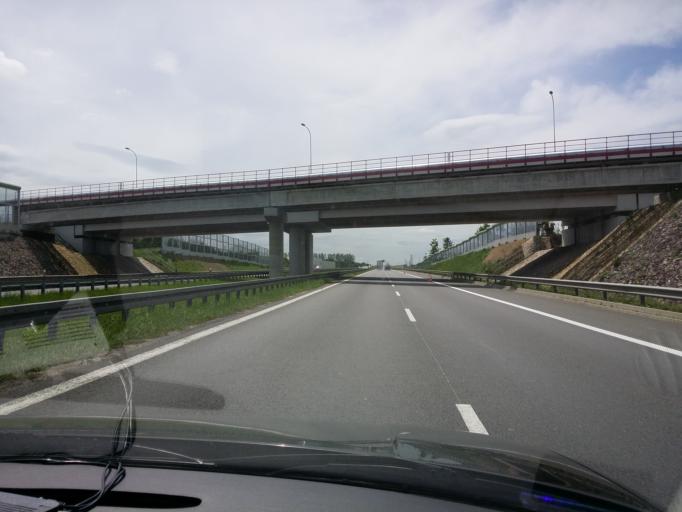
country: PL
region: Masovian Voivodeship
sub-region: Powiat szydlowiecki
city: Szydlowiec
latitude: 51.2191
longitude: 20.8703
